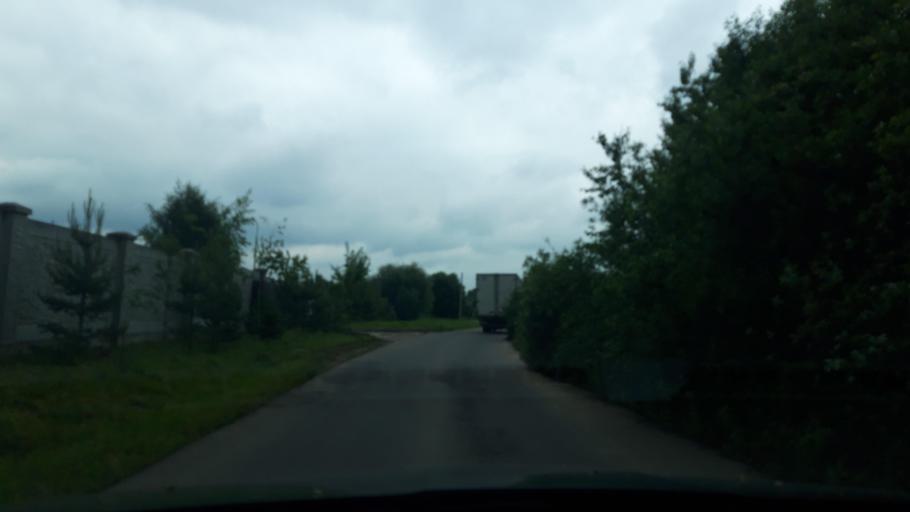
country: RU
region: Moskovskaya
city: Pavlovskaya Sloboda
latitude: 55.7752
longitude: 37.1052
